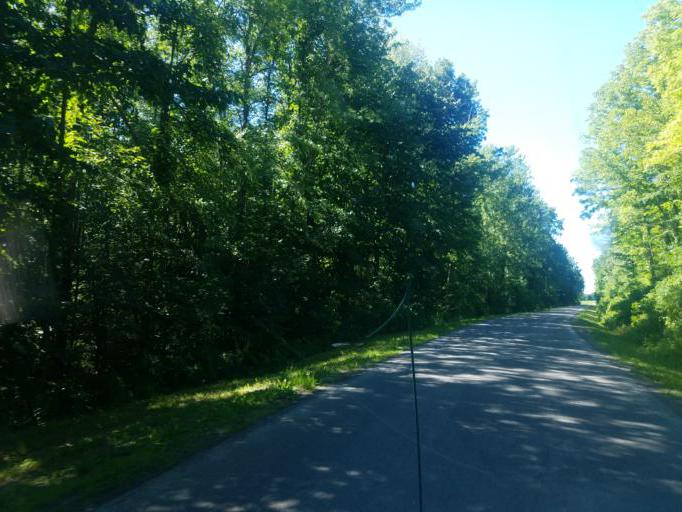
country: US
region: New York
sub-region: Wayne County
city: Lyons
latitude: 43.1000
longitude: -77.0284
